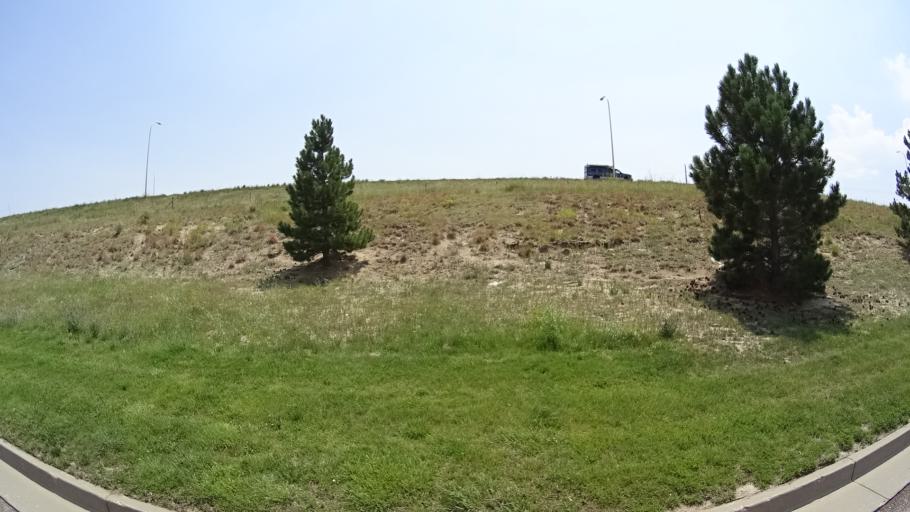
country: US
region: Colorado
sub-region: El Paso County
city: Black Forest
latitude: 38.9430
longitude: -104.7215
